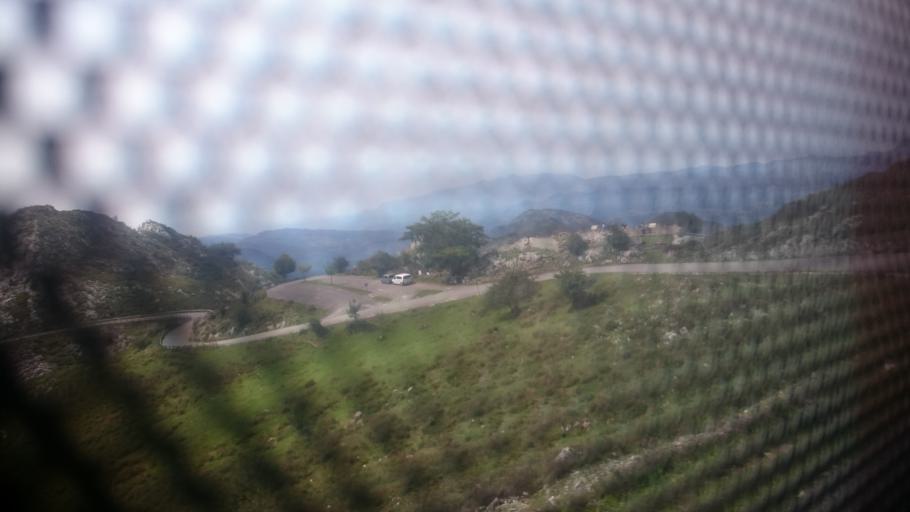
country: ES
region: Asturias
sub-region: Province of Asturias
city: Amieva
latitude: 43.2907
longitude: -5.0071
